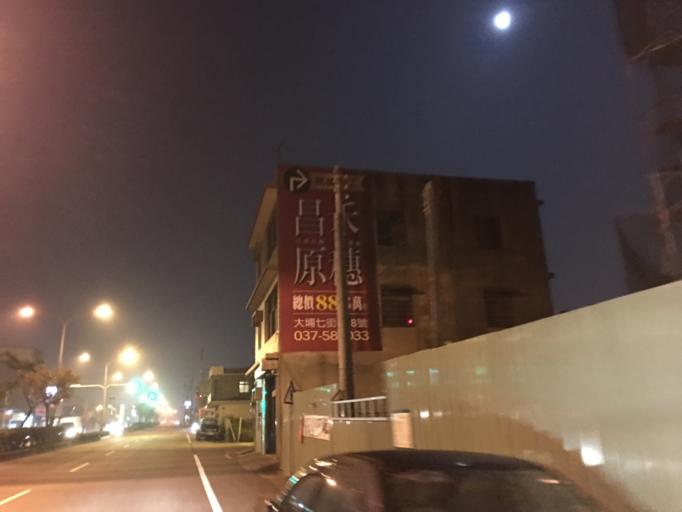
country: TW
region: Taiwan
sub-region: Hsinchu
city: Hsinchu
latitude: 24.7106
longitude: 120.8994
